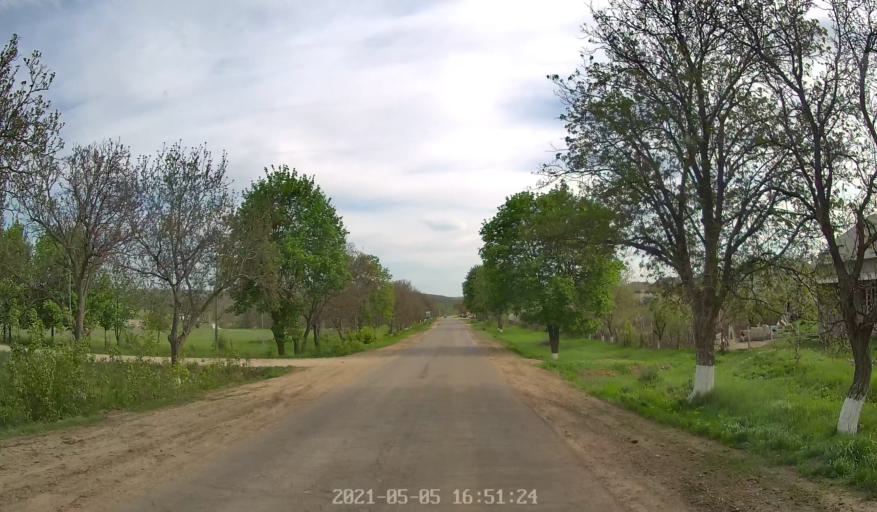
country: MD
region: Chisinau
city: Vadul lui Voda
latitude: 47.0751
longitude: 29.1364
